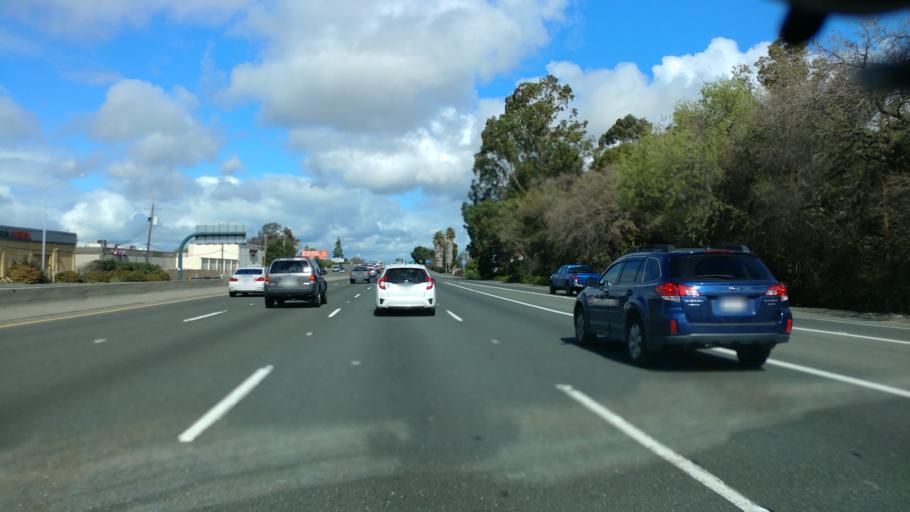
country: US
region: California
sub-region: Contra Costa County
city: Pacheco
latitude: 37.9791
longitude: -122.0651
